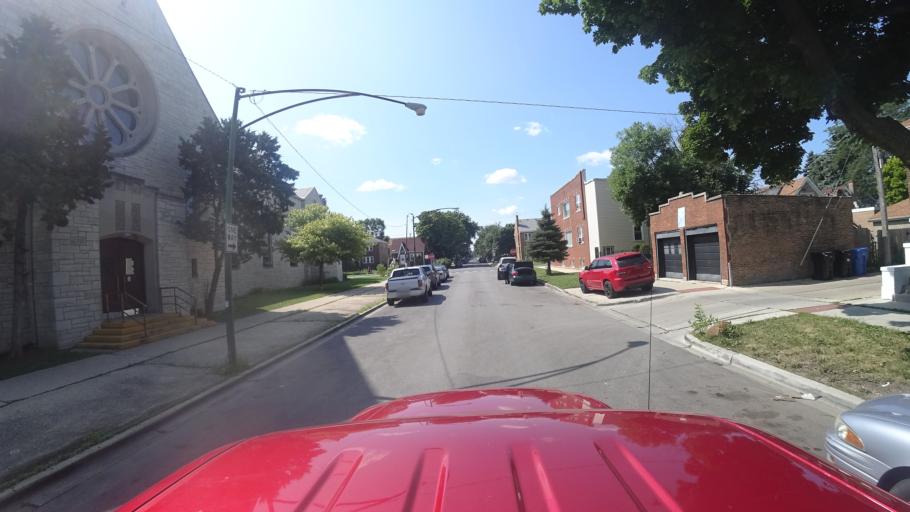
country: US
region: Illinois
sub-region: Cook County
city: Chicago
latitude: 41.7943
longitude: -87.6915
